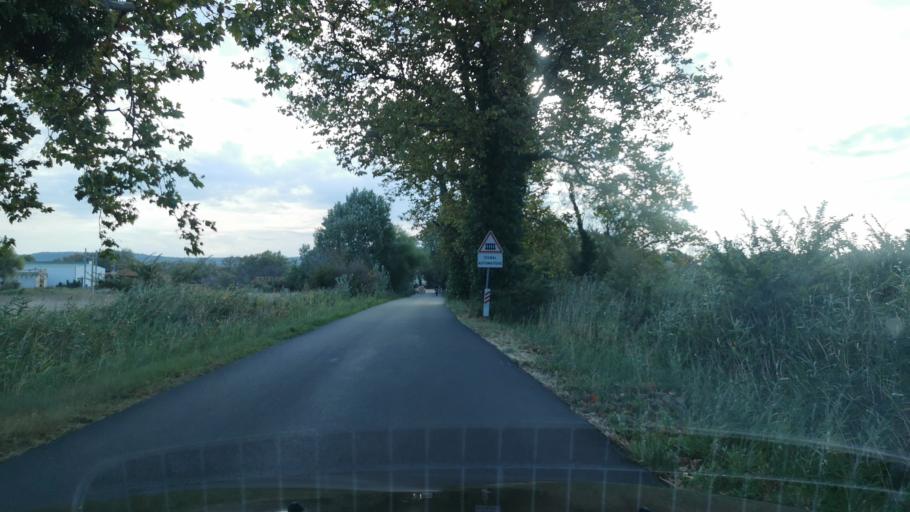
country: FR
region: Languedoc-Roussillon
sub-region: Departement de l'Aude
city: Narbonne
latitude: 43.1303
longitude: 3.0274
